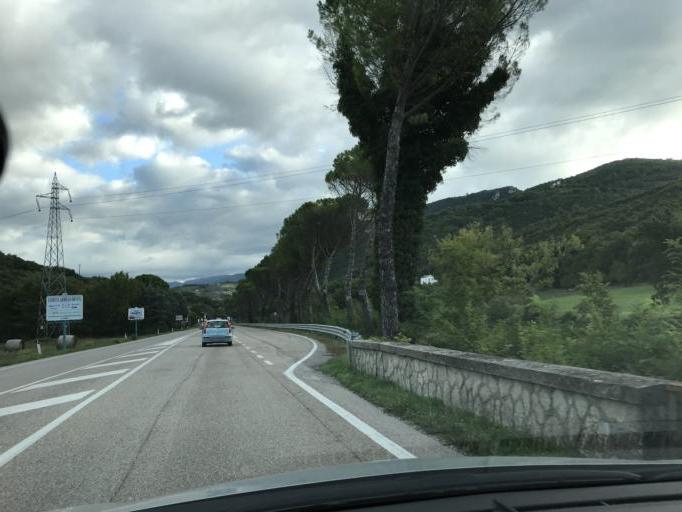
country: IT
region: Umbria
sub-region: Provincia di Perugia
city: Spoleto
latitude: 42.7173
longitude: 12.7258
